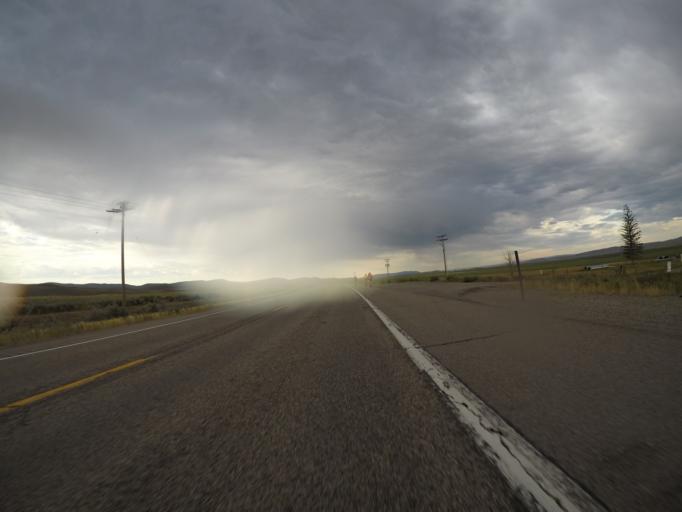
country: US
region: Utah
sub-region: Rich County
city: Randolph
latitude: 41.9328
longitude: -110.9545
